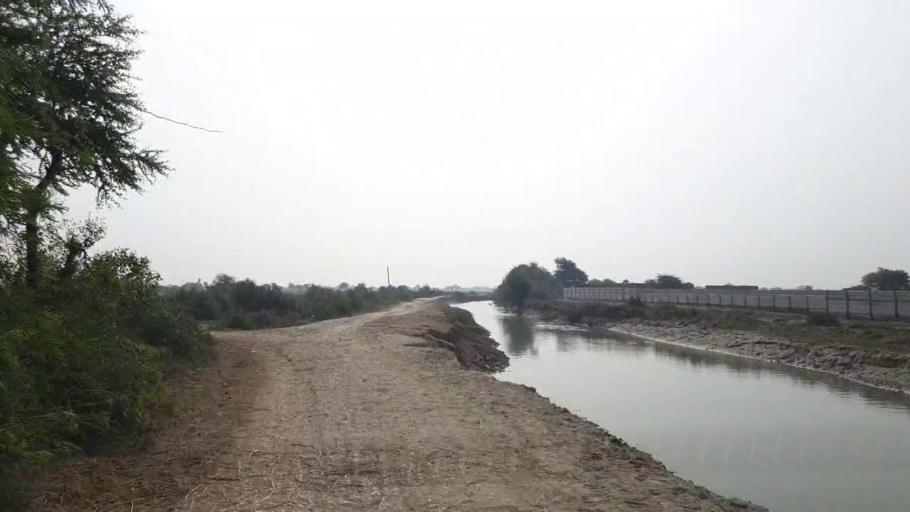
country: PK
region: Sindh
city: Kario
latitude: 24.7910
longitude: 68.5628
